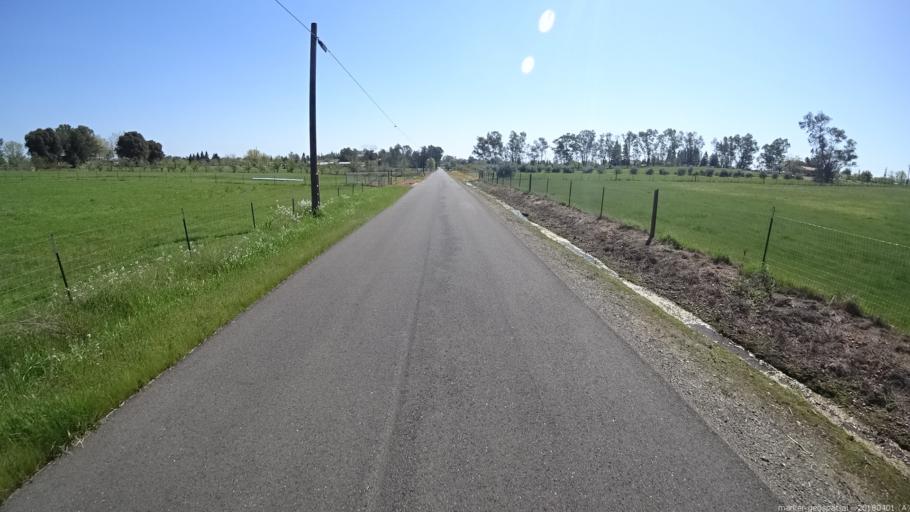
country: US
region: California
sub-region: Sacramento County
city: Wilton
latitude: 38.4131
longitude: -121.2457
